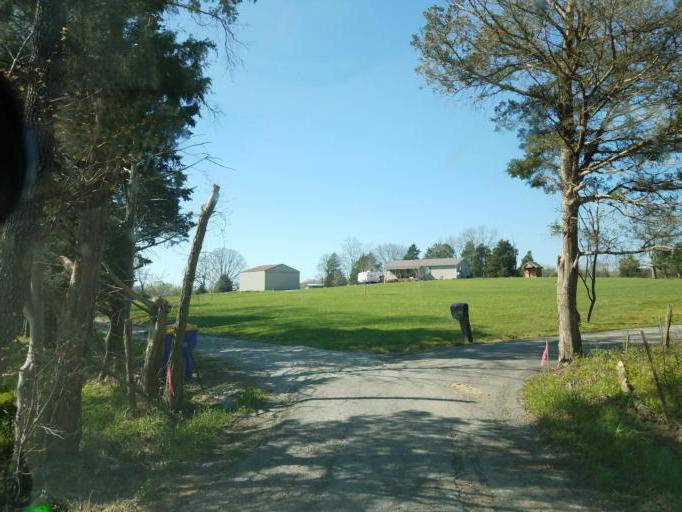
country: US
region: Kentucky
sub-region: Edmonson County
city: Brownsville
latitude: 37.1309
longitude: -86.1516
